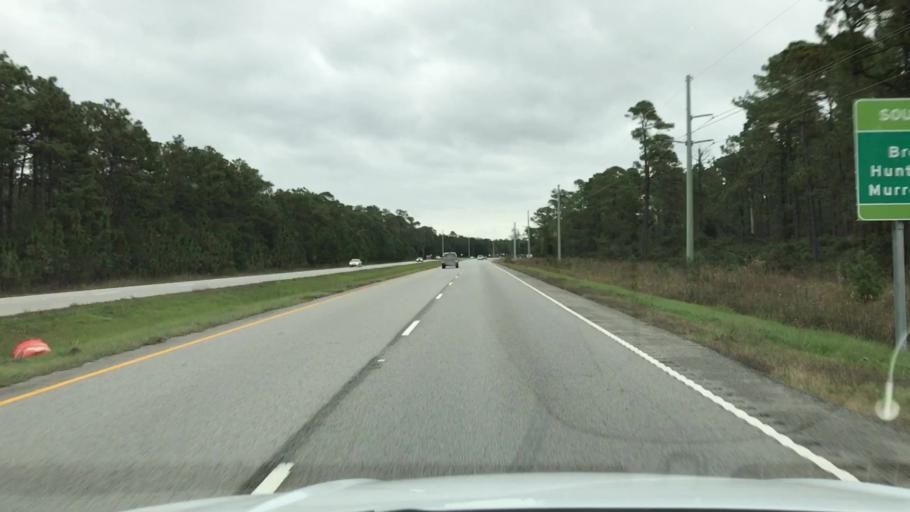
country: US
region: South Carolina
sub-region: Georgetown County
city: Georgetown
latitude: 33.4159
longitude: -79.1835
